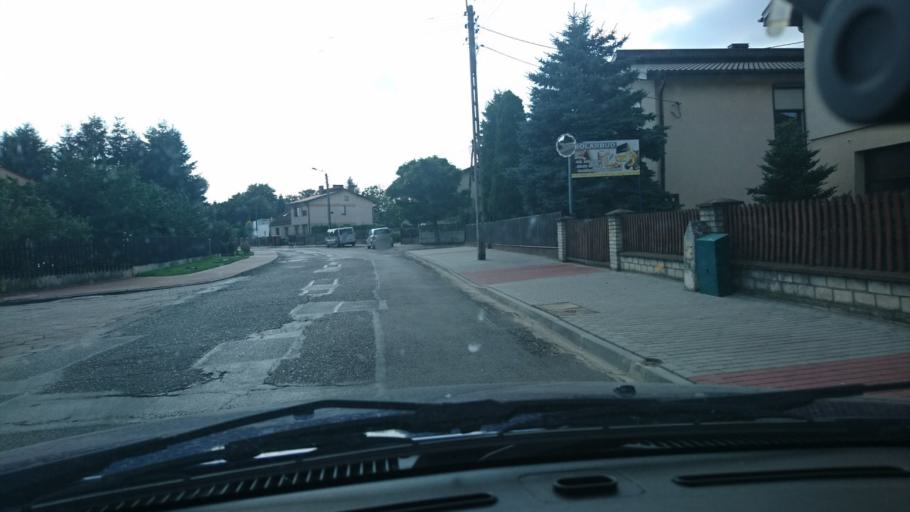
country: PL
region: Greater Poland Voivodeship
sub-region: Powiat ostrowski
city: Odolanow
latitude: 51.5784
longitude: 17.6629
